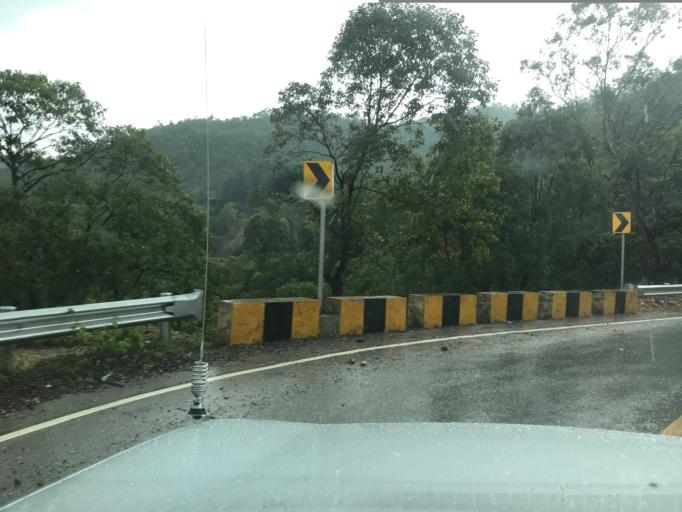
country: TL
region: Aileu
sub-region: Aileu Villa
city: Aileu
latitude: -8.7629
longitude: 125.5563
